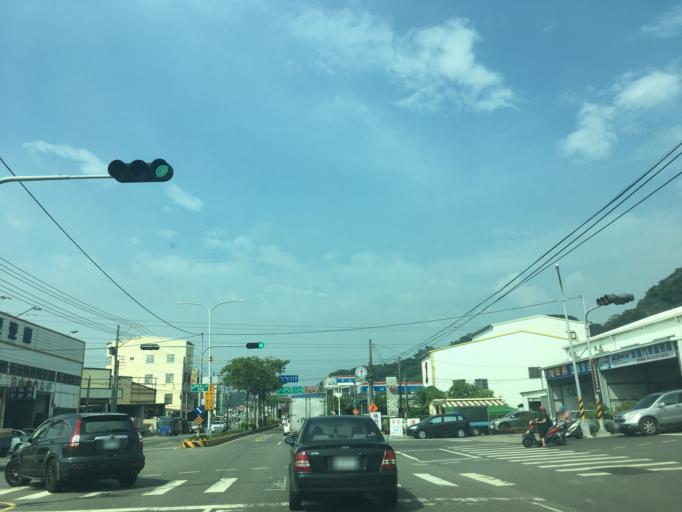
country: TW
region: Taiwan
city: Fengyuan
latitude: 24.2664
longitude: 120.7475
